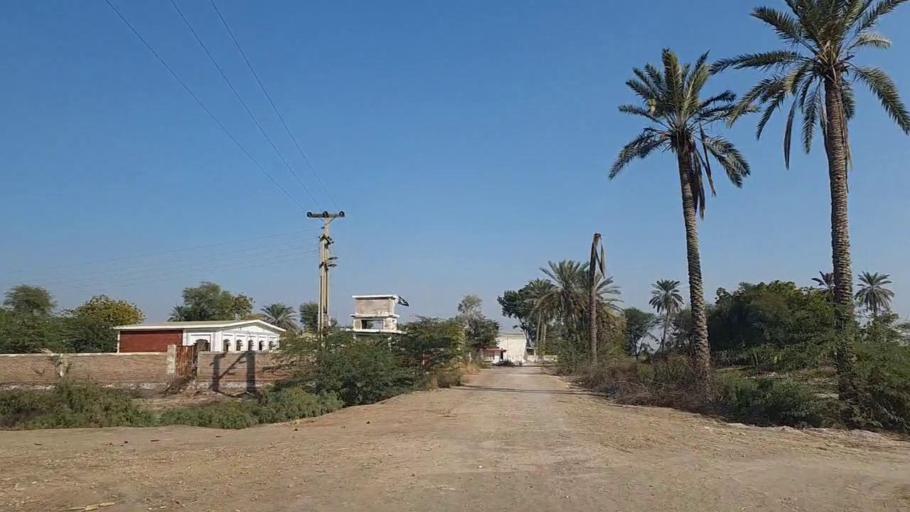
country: PK
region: Sindh
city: Bandhi
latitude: 26.5705
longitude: 68.3108
